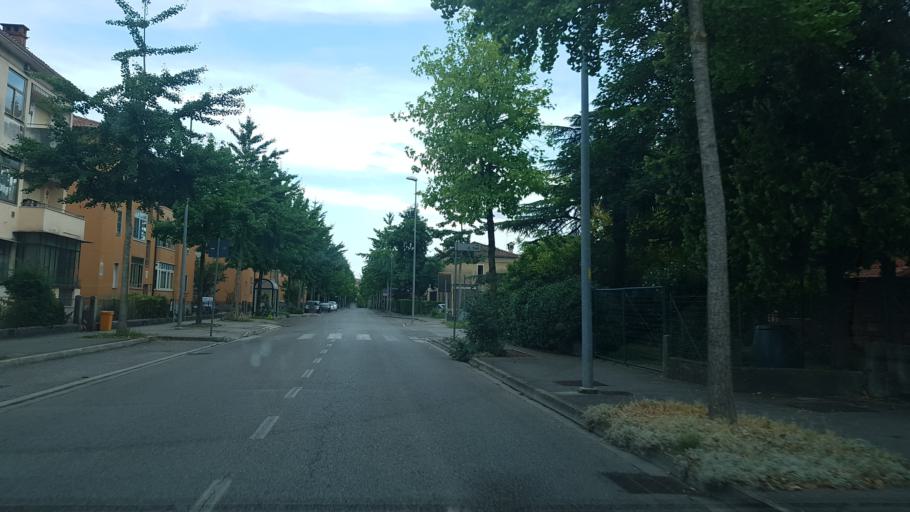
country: IT
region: Friuli Venezia Giulia
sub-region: Provincia di Gorizia
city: Gorizia
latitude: 45.9479
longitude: 13.6078
